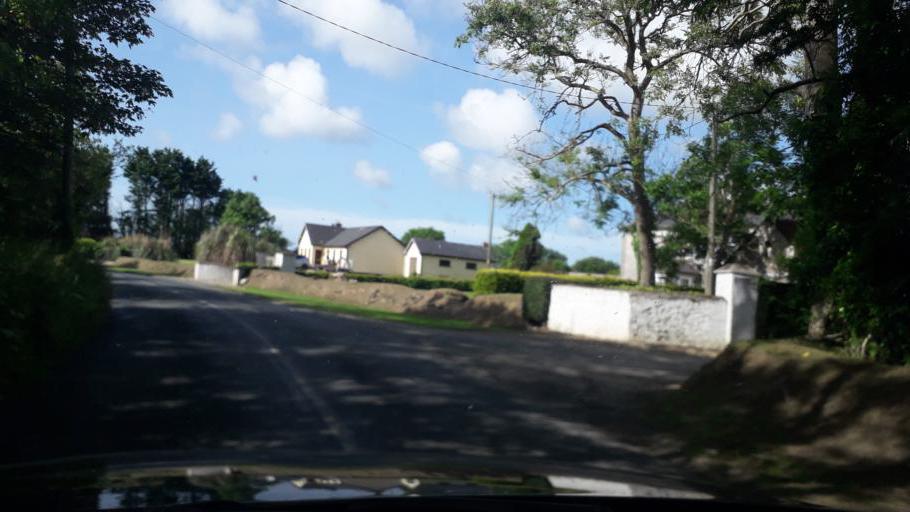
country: IE
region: Leinster
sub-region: Loch Garman
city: Loch Garman
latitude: 52.2553
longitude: -6.5520
